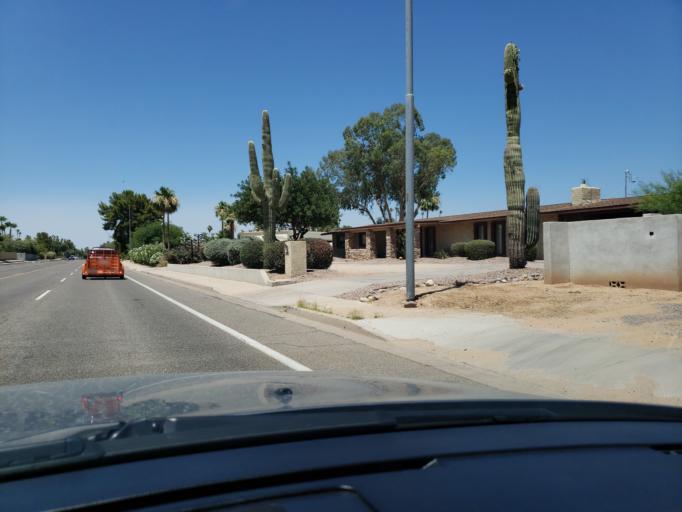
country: US
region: Arizona
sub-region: Maricopa County
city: Paradise Valley
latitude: 33.5994
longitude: -111.9433
